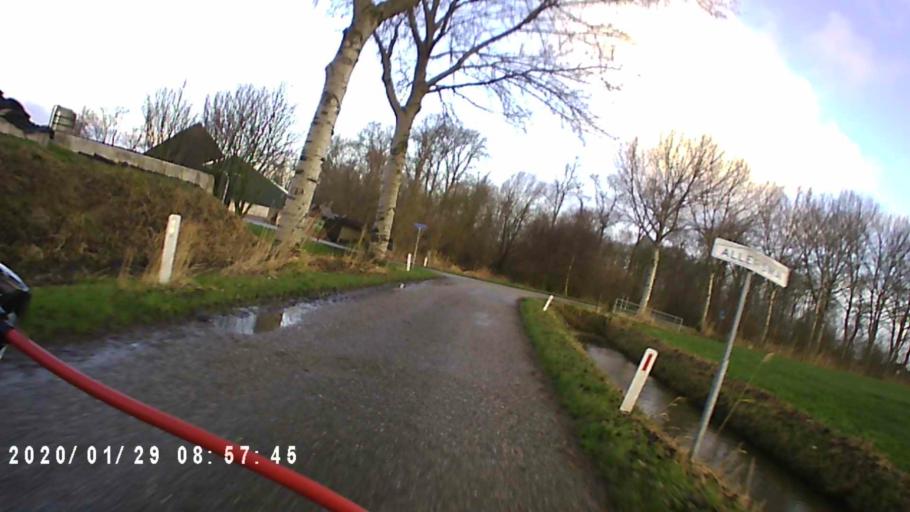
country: NL
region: Groningen
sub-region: Gemeente Zuidhorn
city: Oldehove
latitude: 53.3171
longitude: 6.4541
